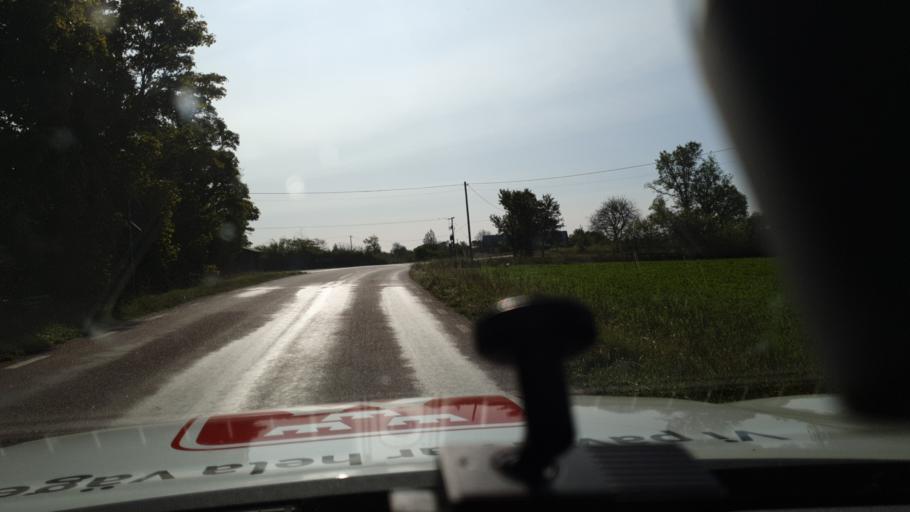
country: SE
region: Gotland
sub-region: Gotland
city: Hemse
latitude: 57.1510
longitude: 18.2833
